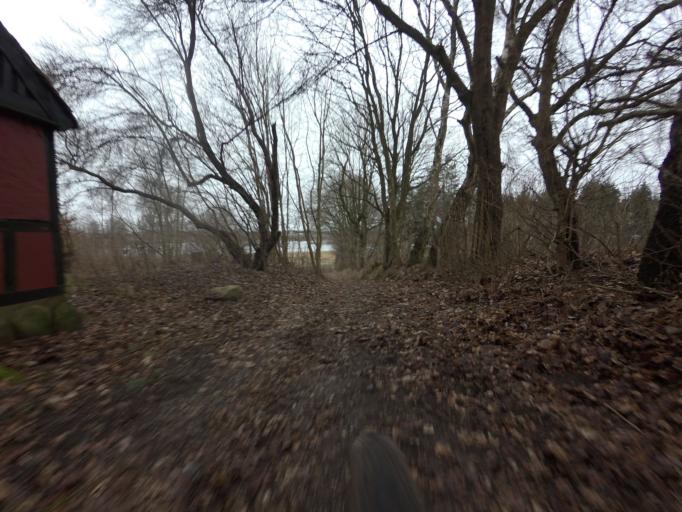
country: DK
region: Central Jutland
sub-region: Arhus Kommune
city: Kolt
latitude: 56.1364
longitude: 10.0672
